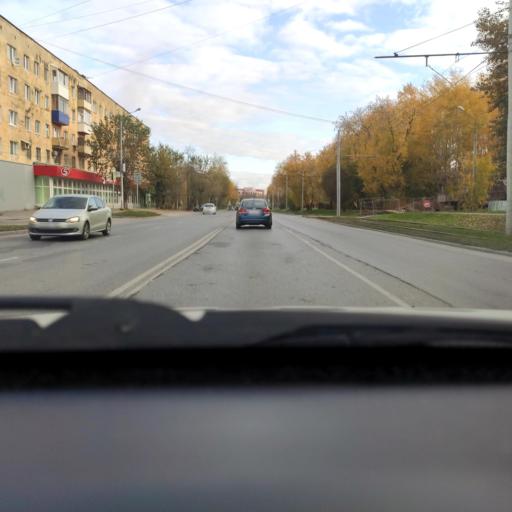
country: RU
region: Perm
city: Perm
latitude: 58.0228
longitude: 56.2862
